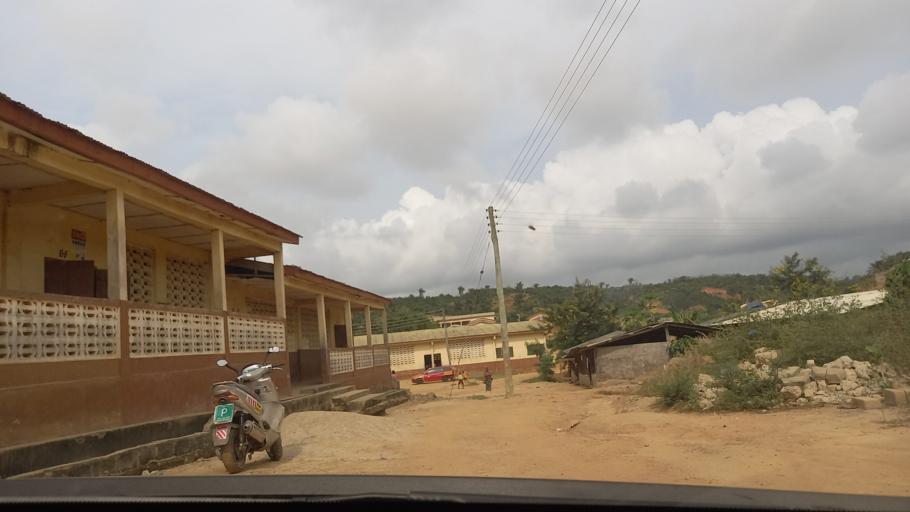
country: GH
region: Western
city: Shama Junction
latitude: 4.9864
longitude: -1.6399
